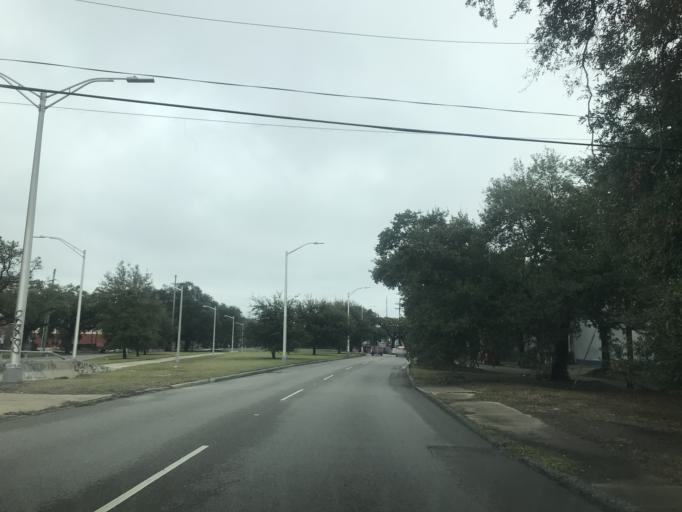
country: US
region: Louisiana
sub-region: Orleans Parish
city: New Orleans
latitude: 29.9640
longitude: -90.0994
